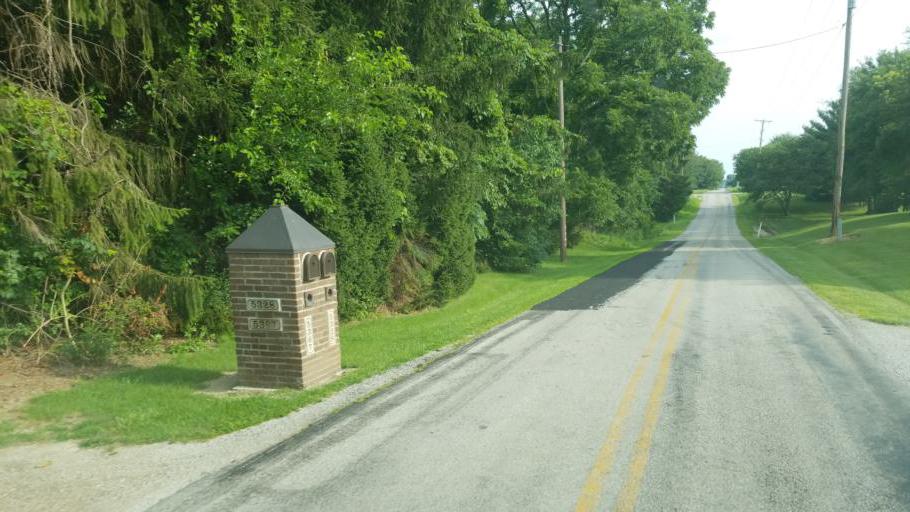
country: US
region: Ohio
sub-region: Delaware County
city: Ashley
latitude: 40.4820
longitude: -83.0538
